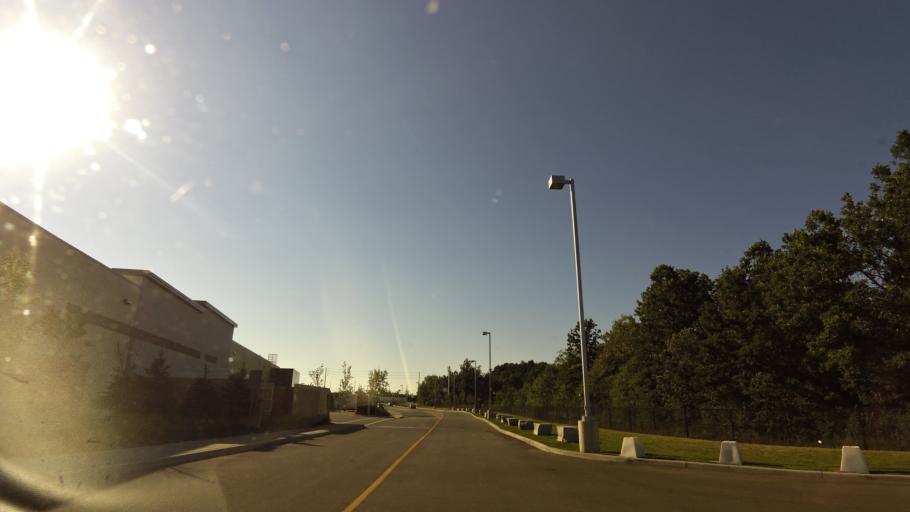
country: CA
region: Ontario
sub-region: Halton
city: Milton
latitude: 43.5764
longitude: -79.8277
